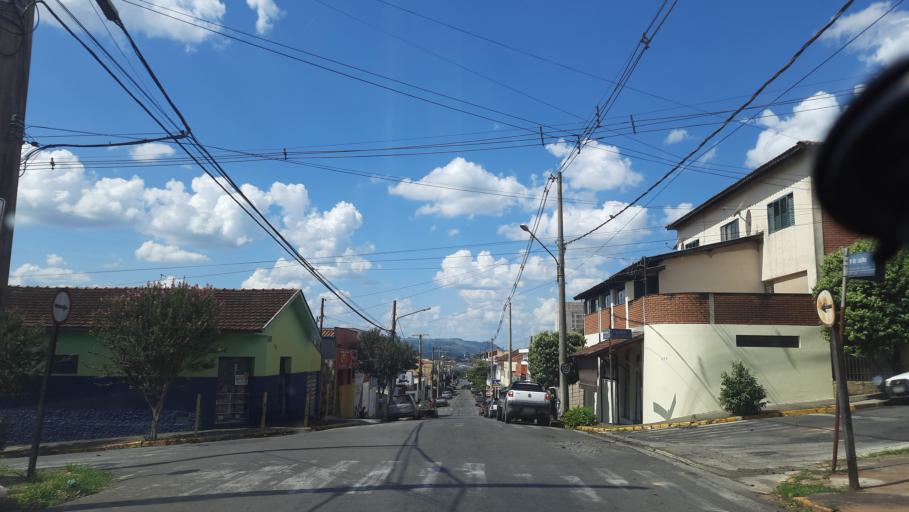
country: BR
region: Sao Paulo
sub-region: Sao Jose Do Rio Pardo
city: Sao Jose do Rio Pardo
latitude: -21.6033
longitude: -46.8975
